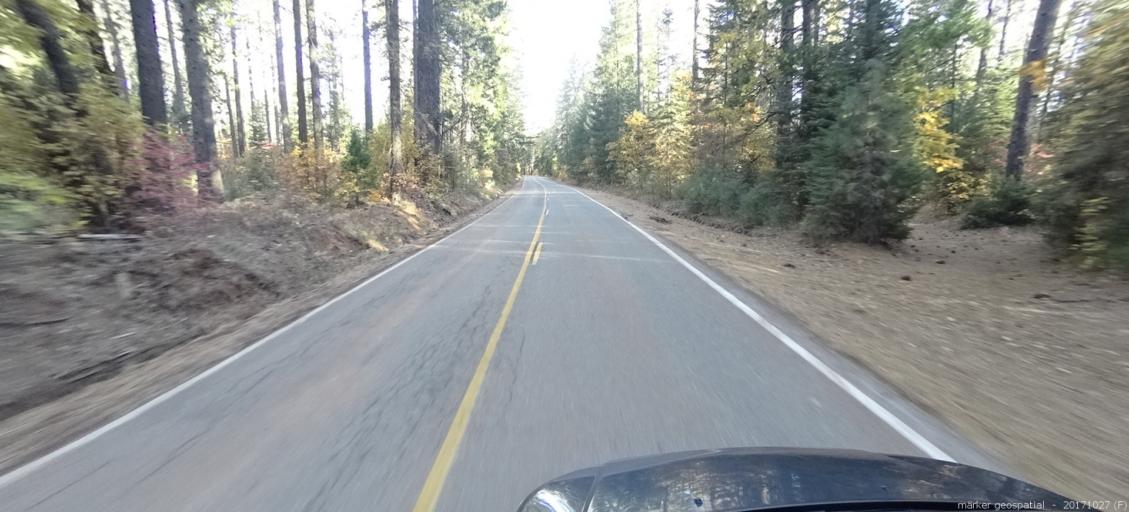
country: US
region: California
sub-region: Shasta County
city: Burney
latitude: 40.9355
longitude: -121.9487
